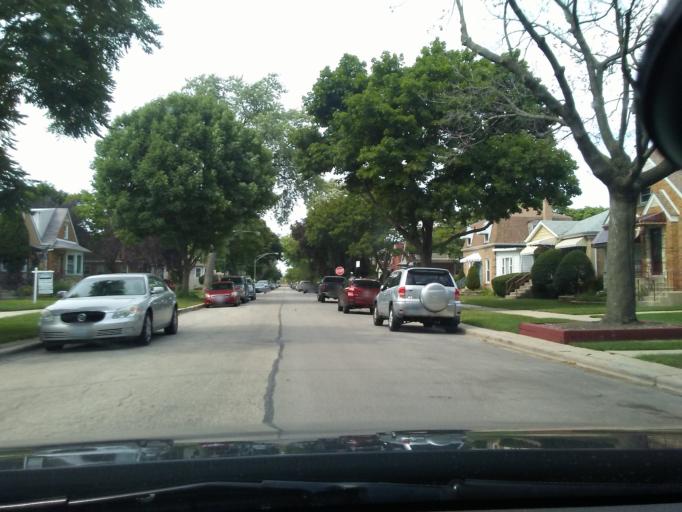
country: US
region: Illinois
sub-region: Cook County
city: Harwood Heights
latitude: 41.9787
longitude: -87.7836
